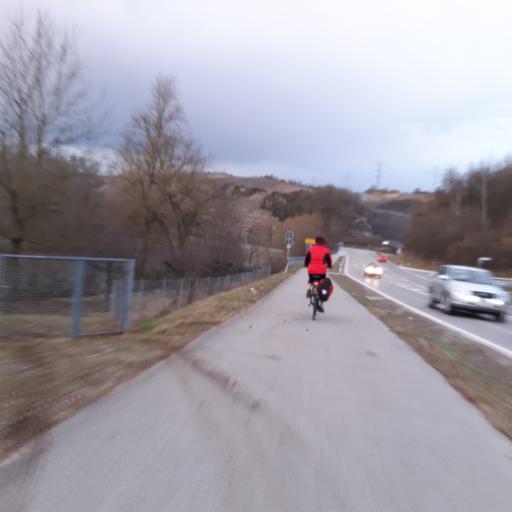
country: DE
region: Baden-Wuerttemberg
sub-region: Regierungsbezirk Stuttgart
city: Pleidelsheim
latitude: 48.9762
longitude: 9.2146
